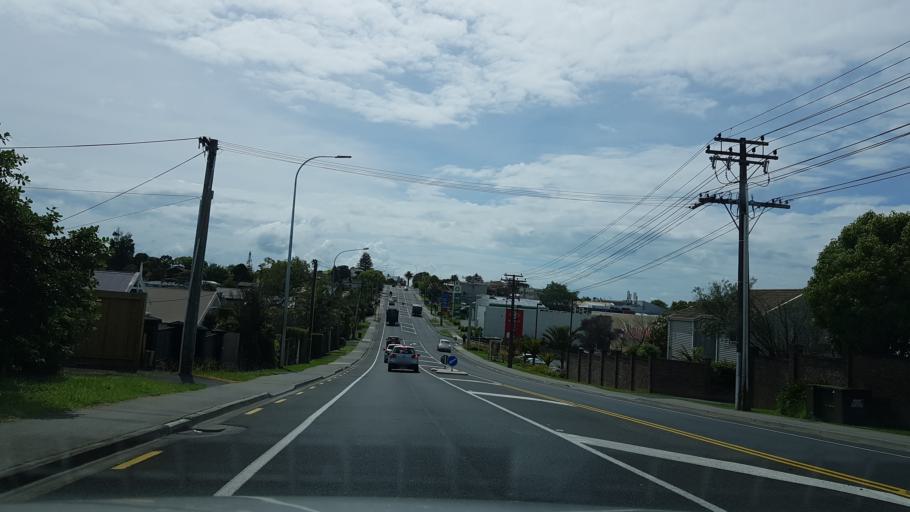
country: NZ
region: Auckland
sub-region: Auckland
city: North Shore
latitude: -36.8108
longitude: 174.7105
